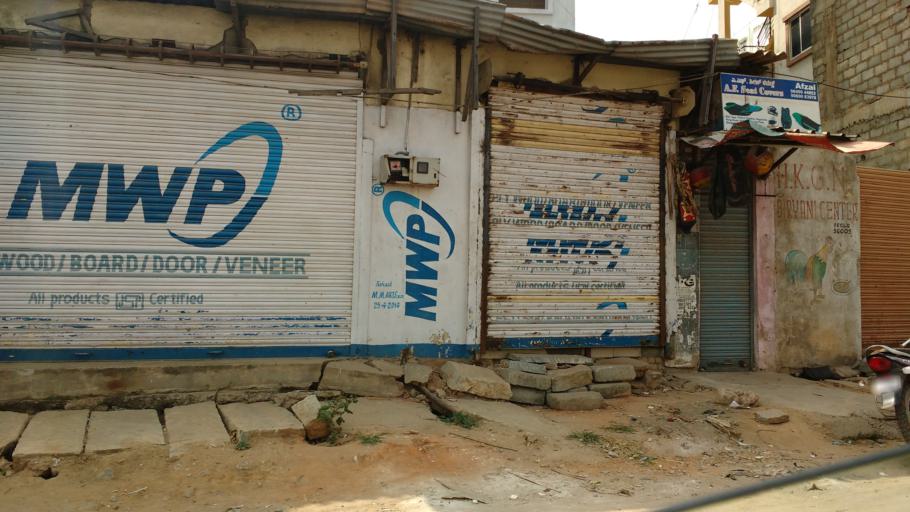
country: IN
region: Karnataka
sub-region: Bangalore Urban
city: Yelahanka
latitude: 13.0412
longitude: 77.6225
